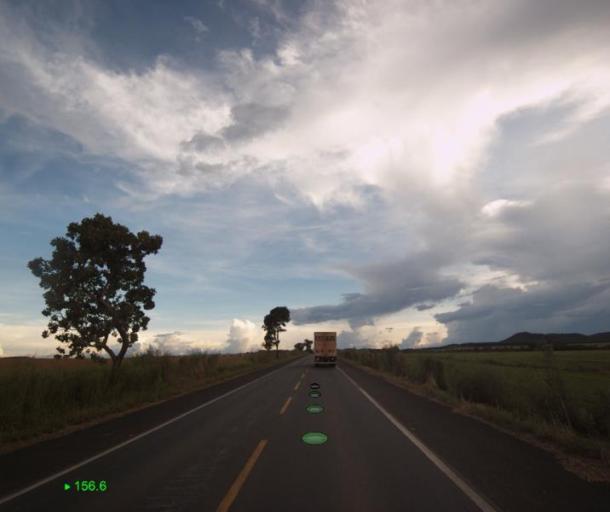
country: BR
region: Goias
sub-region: Uruacu
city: Uruacu
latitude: -14.1431
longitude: -49.1161
